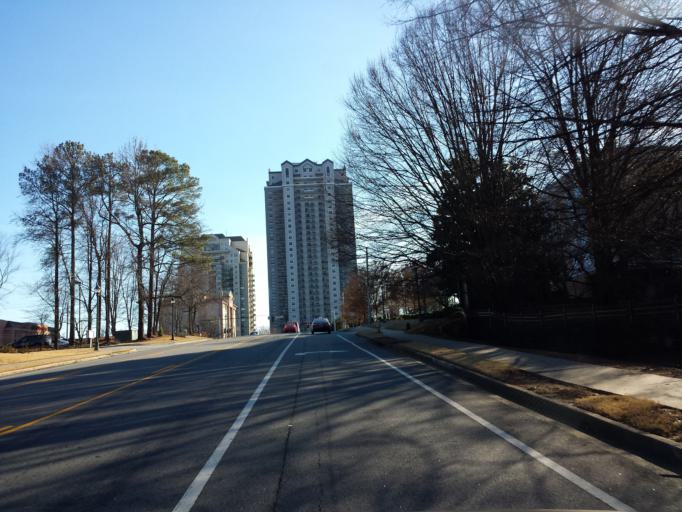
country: US
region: Georgia
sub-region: Fulton County
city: Sandy Springs
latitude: 33.9204
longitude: -84.3600
